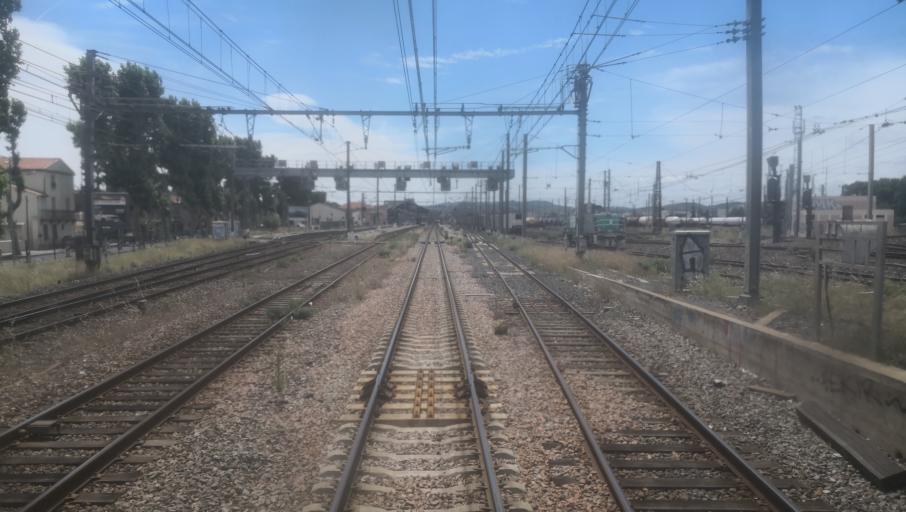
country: FR
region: Languedoc-Roussillon
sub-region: Departement de l'Aude
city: Narbonne
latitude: 43.1938
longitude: 3.0092
